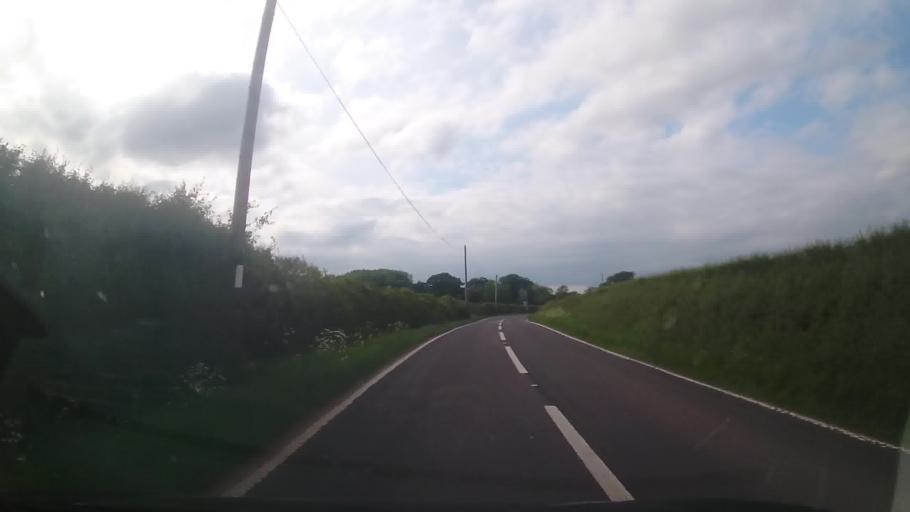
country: GB
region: England
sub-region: Shropshire
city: Petton
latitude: 52.8210
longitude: -2.7973
